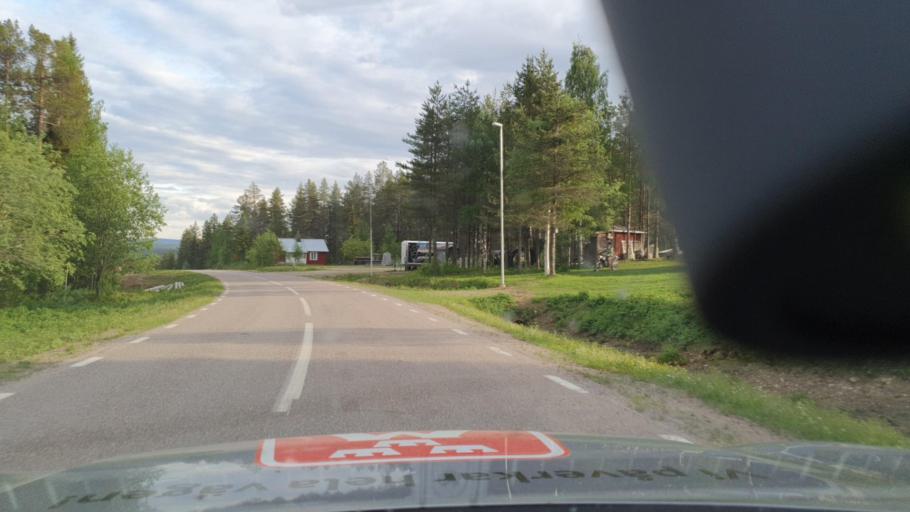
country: SE
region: Norrbotten
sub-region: Gallivare Kommun
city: Gaellivare
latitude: 66.9586
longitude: 21.2346
